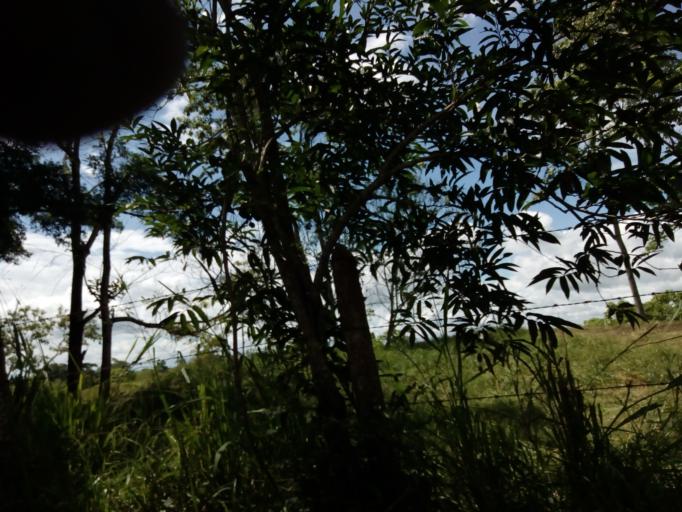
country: CO
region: Boyaca
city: Puerto Boyaca
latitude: 5.9632
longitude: -74.4528
